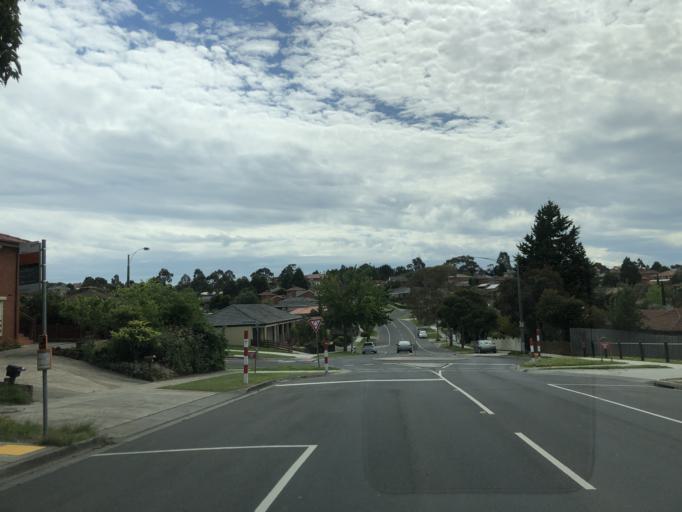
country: AU
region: Victoria
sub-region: Casey
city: Endeavour Hills
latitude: -37.9795
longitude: 145.2690
